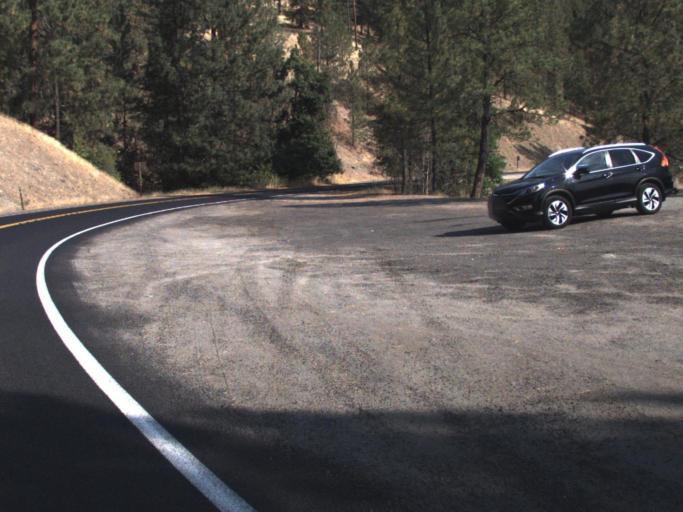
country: US
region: Washington
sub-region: Spokane County
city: Deer Park
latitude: 47.8840
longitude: -117.6979
